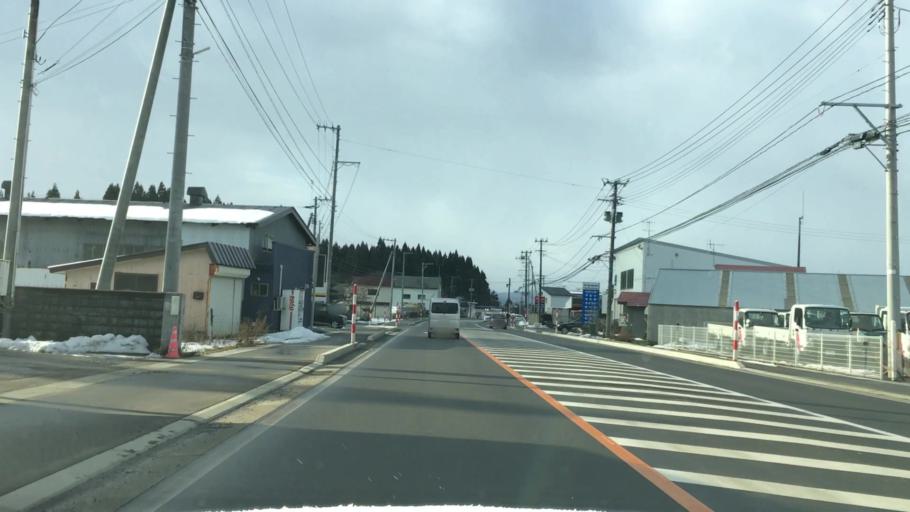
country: JP
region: Akita
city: Odate
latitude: 40.3092
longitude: 140.5694
